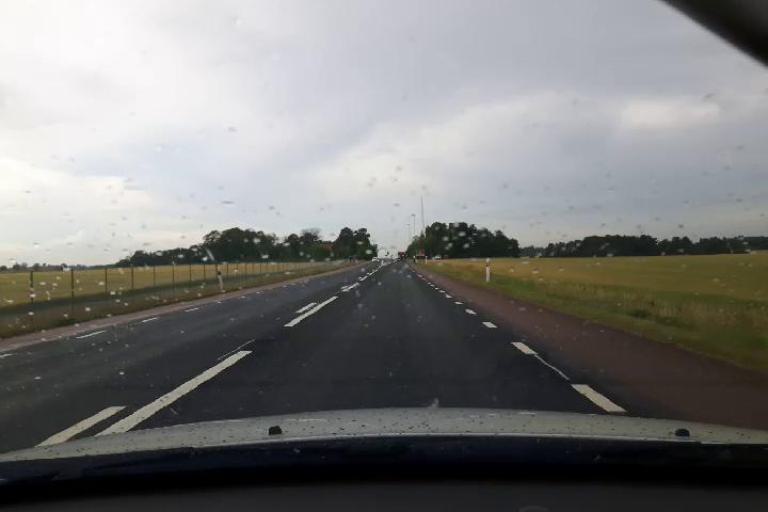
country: SE
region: Uppsala
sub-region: Uppsala Kommun
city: Gamla Uppsala
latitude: 59.9558
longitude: 17.5857
